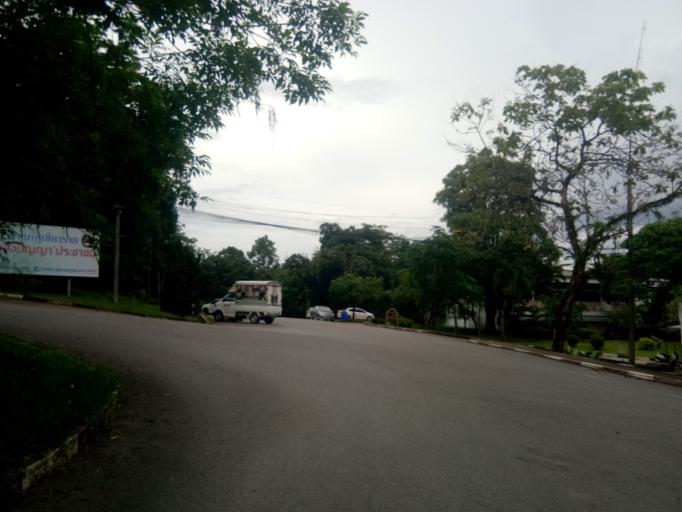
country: TH
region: Chiang Rai
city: Chiang Rai
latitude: 19.9802
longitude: 99.8504
